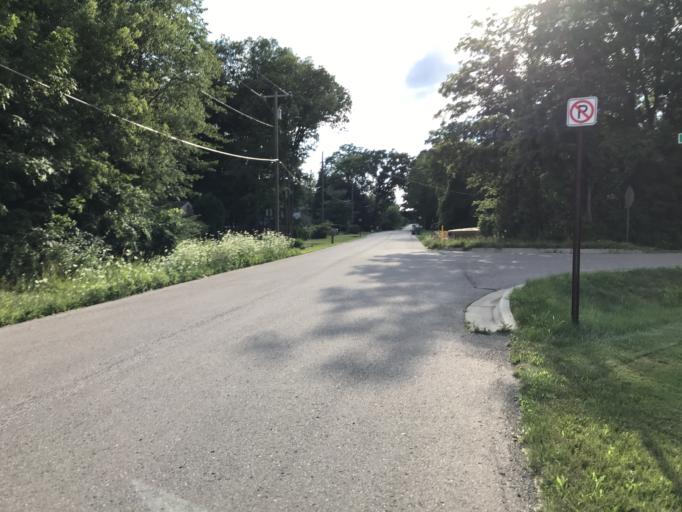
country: US
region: Michigan
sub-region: Oakland County
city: Farmington
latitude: 42.4656
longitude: -83.3512
